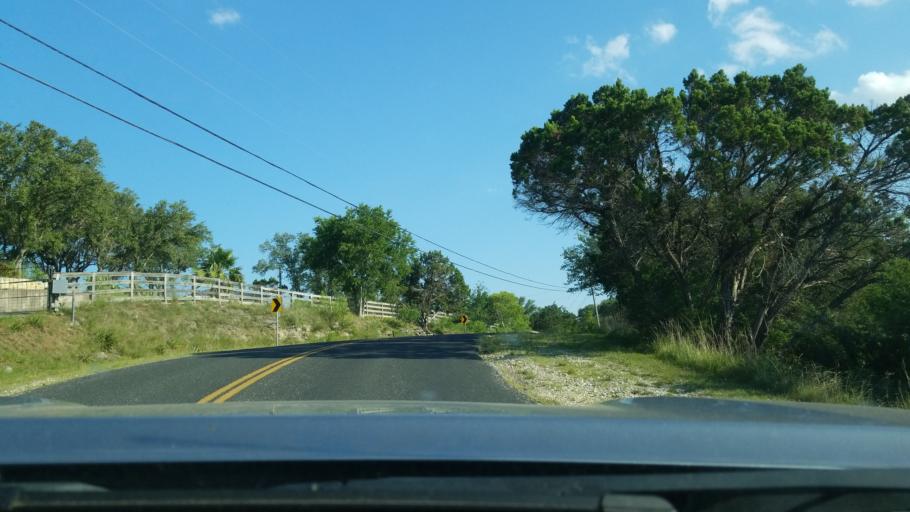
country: US
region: Texas
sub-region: Comal County
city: Bulverde
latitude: 29.7129
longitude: -98.4368
